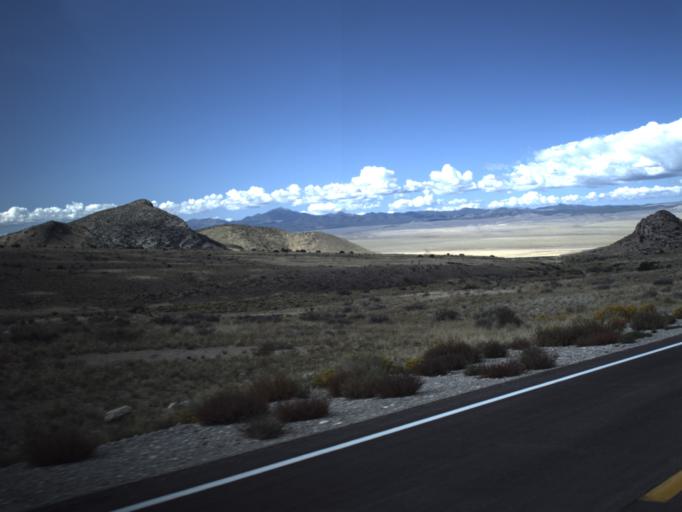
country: US
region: Utah
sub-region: Beaver County
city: Milford
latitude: 38.5131
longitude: -113.5777
